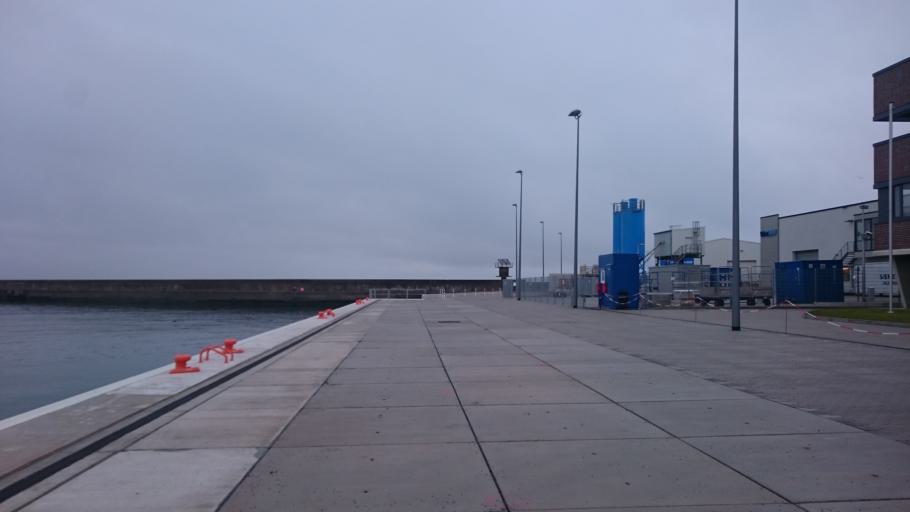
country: DE
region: Schleswig-Holstein
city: Helgoland
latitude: 54.1735
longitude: 7.8919
